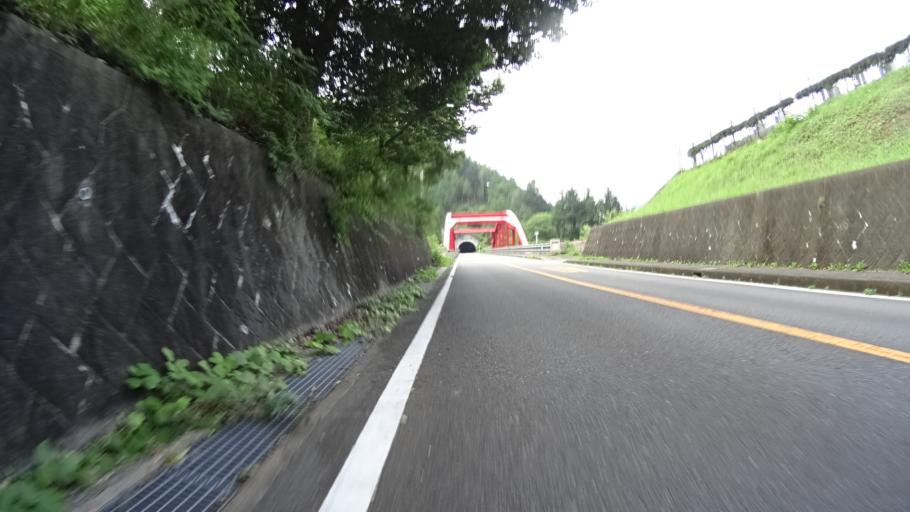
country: JP
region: Kanagawa
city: Hadano
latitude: 35.5086
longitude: 139.2310
